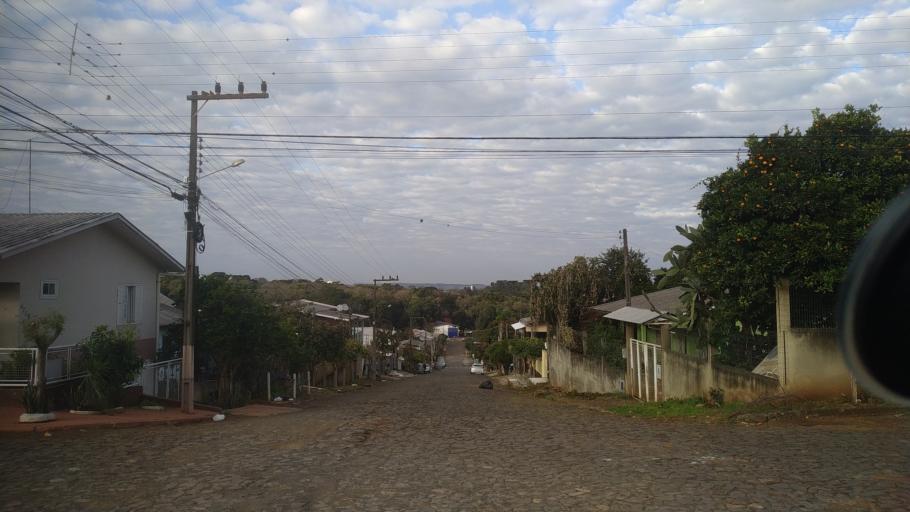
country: BR
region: Santa Catarina
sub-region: Chapeco
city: Chapeco
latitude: -27.0986
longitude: -52.6772
